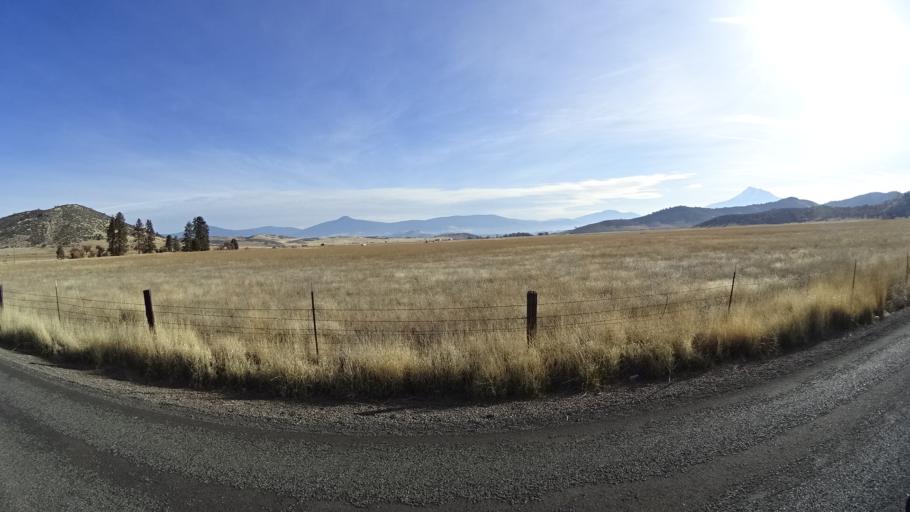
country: US
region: California
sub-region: Siskiyou County
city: Montague
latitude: 41.6545
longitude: -122.5830
